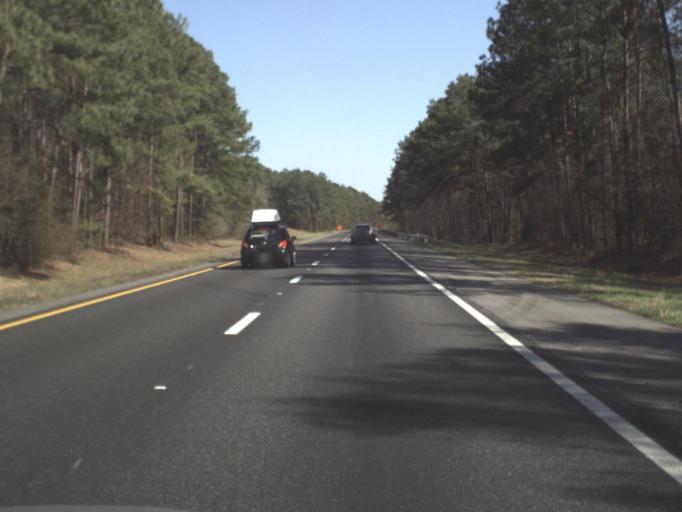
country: US
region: Florida
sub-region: Gadsden County
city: Chattahoochee
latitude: 30.6302
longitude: -84.8649
